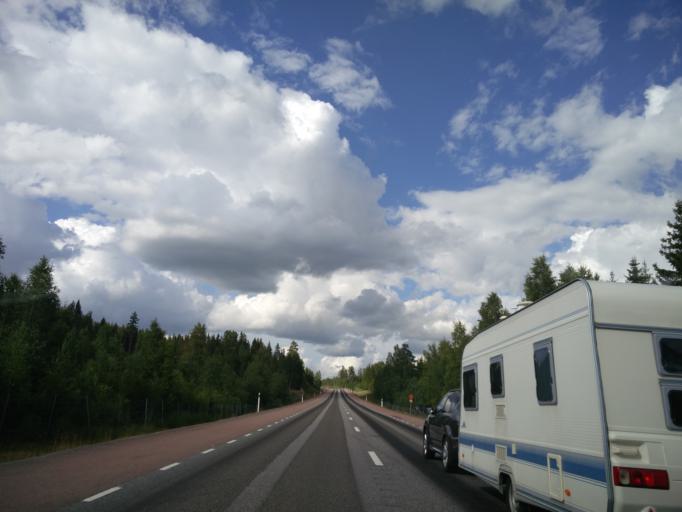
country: SE
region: Vaermland
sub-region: Torsby Kommun
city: Torsby
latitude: 60.1882
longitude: 13.0183
